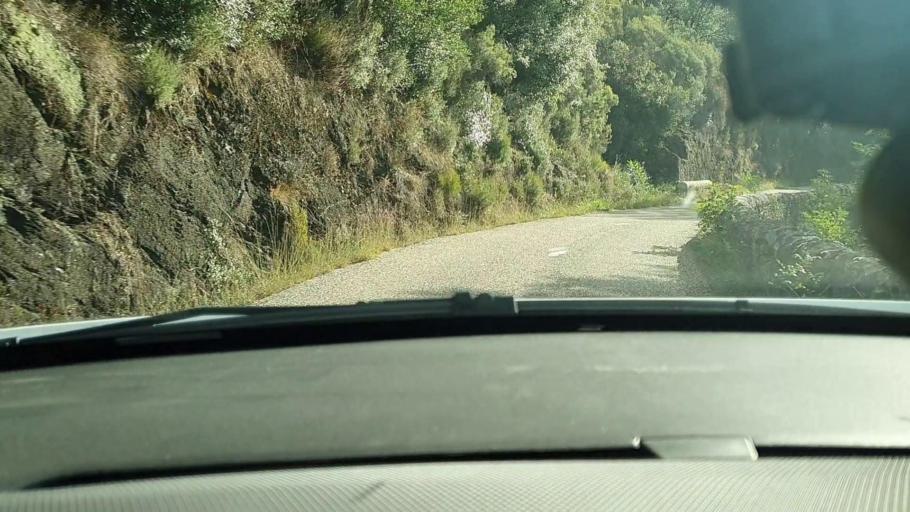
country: FR
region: Languedoc-Roussillon
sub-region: Departement du Gard
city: Besseges
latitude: 44.3574
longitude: 3.9957
